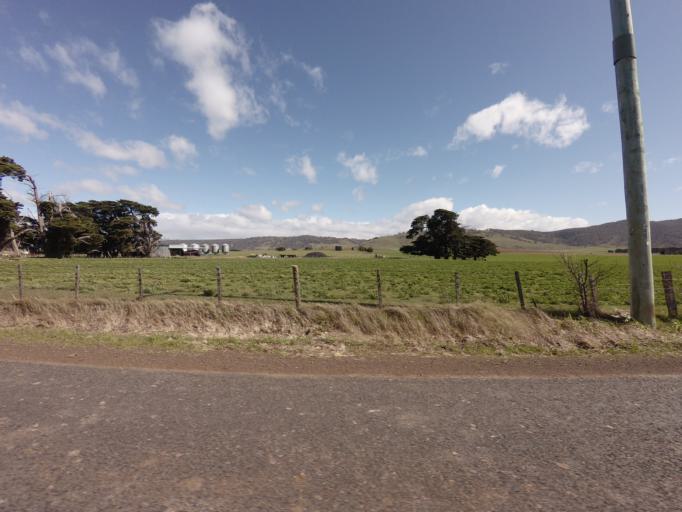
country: AU
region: Tasmania
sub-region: Northern Midlands
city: Evandale
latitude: -42.0121
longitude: 147.4599
